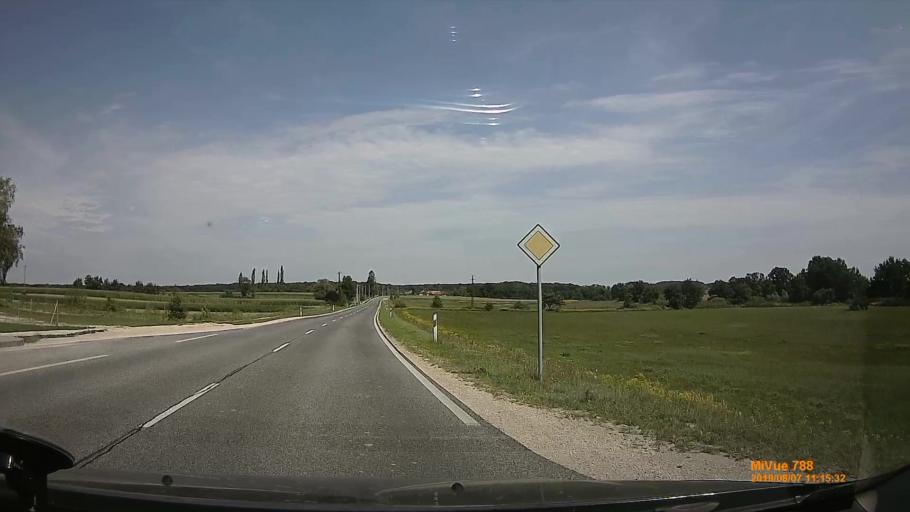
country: HU
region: Zala
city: Lenti
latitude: 46.7176
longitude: 16.5504
